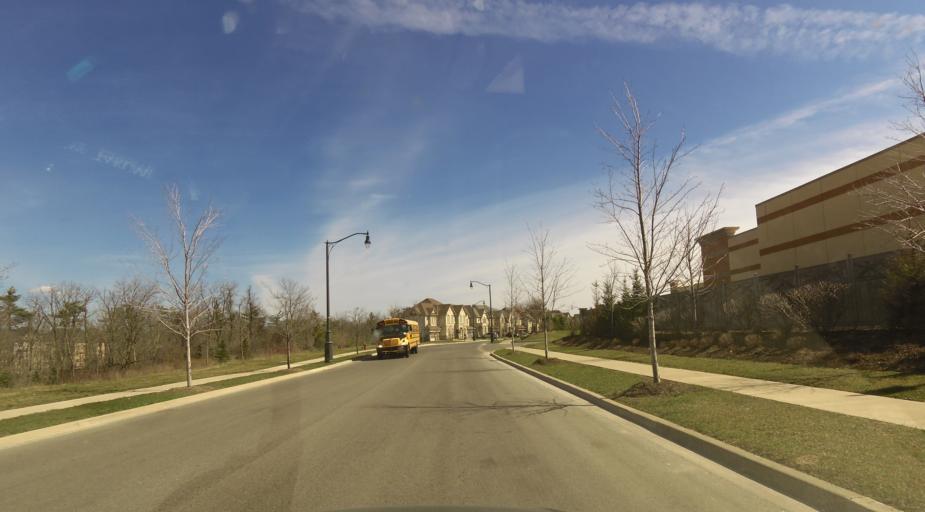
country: CA
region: Ontario
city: Brampton
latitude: 43.6588
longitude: -79.8119
